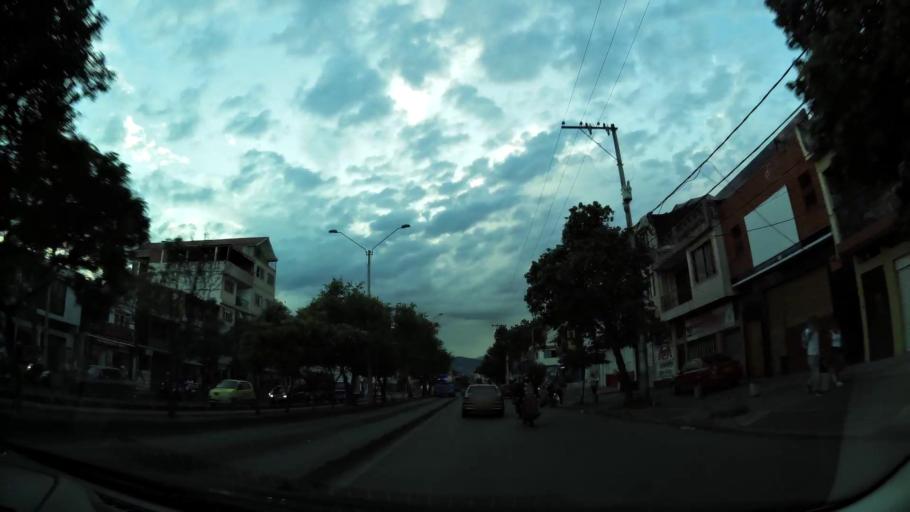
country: CO
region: Valle del Cauca
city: Cali
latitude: 3.4448
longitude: -76.5071
